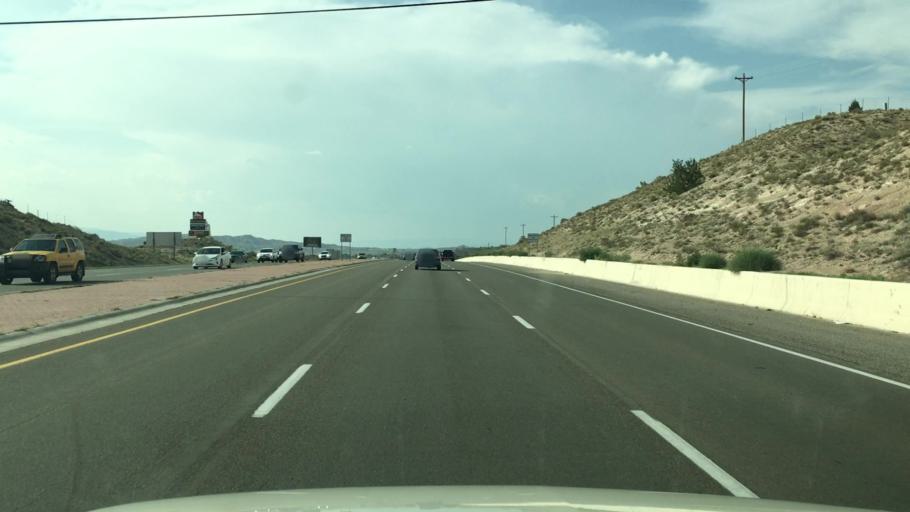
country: US
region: New Mexico
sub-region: Santa Fe County
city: Pojoaque
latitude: 35.8704
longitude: -106.0045
